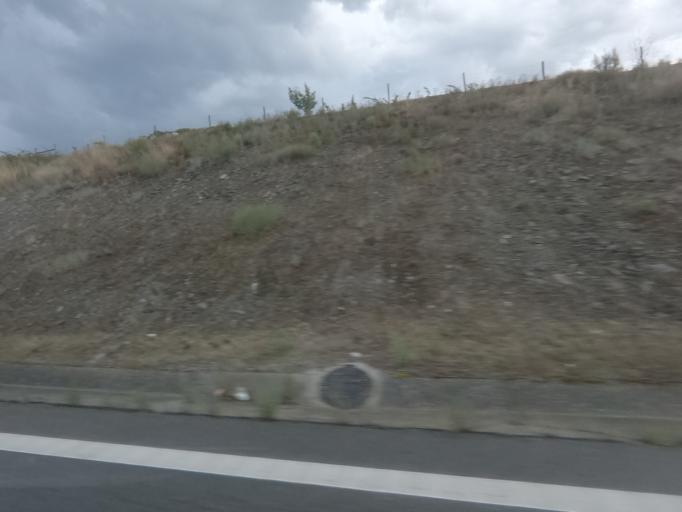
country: PT
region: Vila Real
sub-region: Santa Marta de Penaguiao
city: Santa Marta de Penaguiao
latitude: 41.2059
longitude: -7.7436
